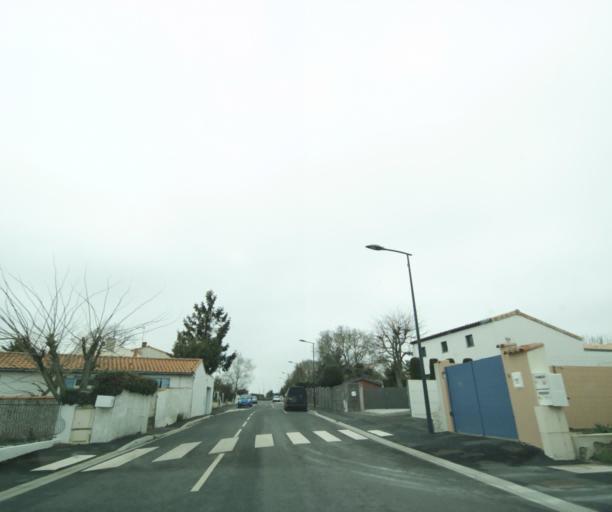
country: FR
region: Poitou-Charentes
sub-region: Departement de la Charente-Maritime
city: Lagord
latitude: 46.1832
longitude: -1.1429
